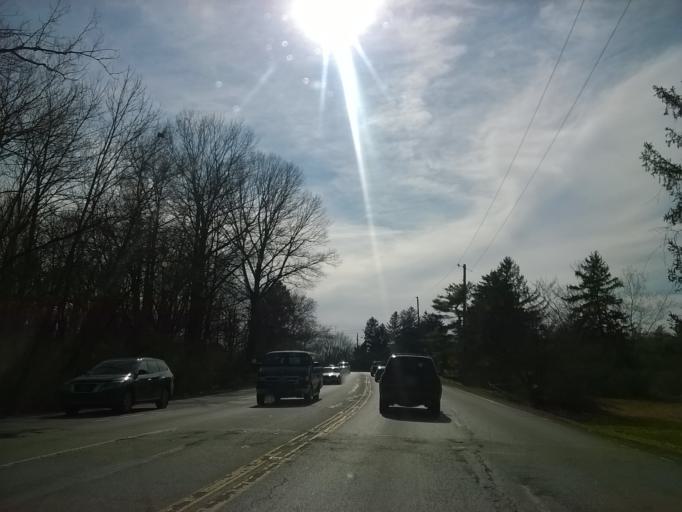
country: US
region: Indiana
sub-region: Marion County
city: Meridian Hills
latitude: 39.8553
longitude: -86.1965
